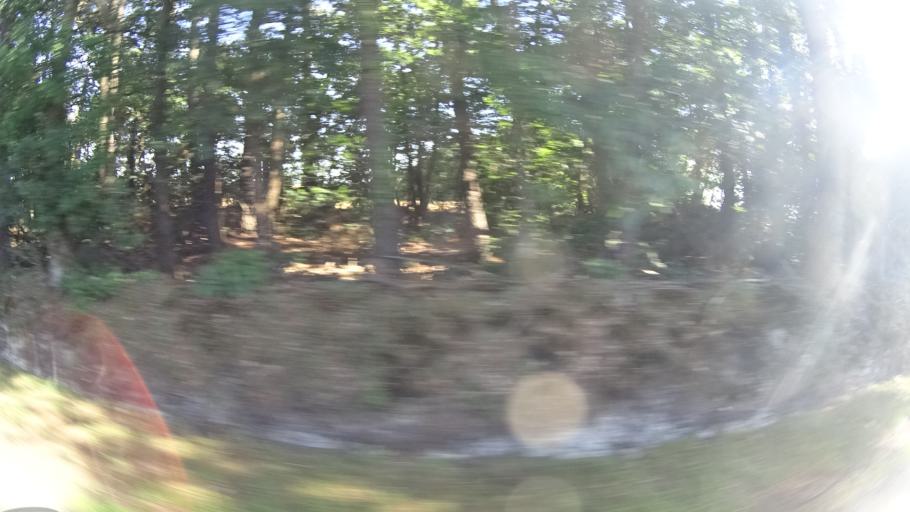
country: FR
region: Brittany
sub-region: Departement d'Ille-et-Vilaine
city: Langon
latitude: 47.7414
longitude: -1.8130
